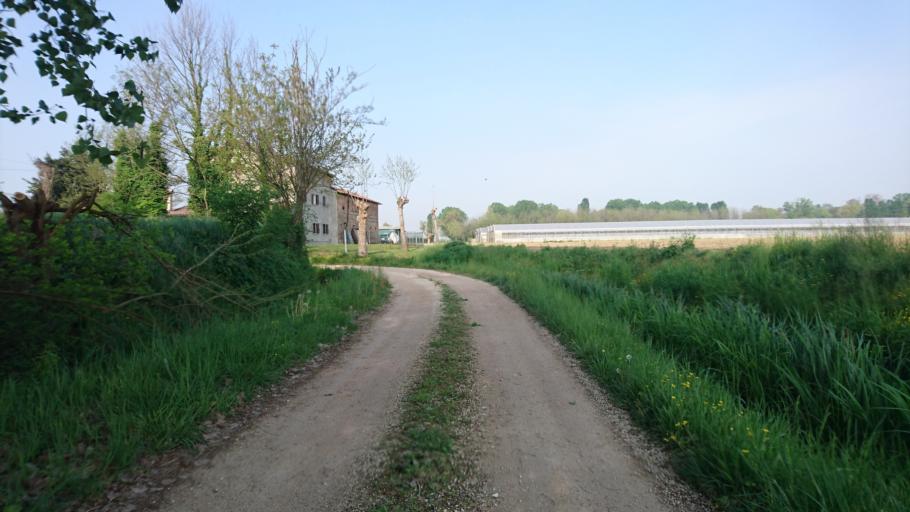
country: IT
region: Veneto
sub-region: Provincia di Padova
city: Albignasego
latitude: 45.3556
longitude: 11.9001
